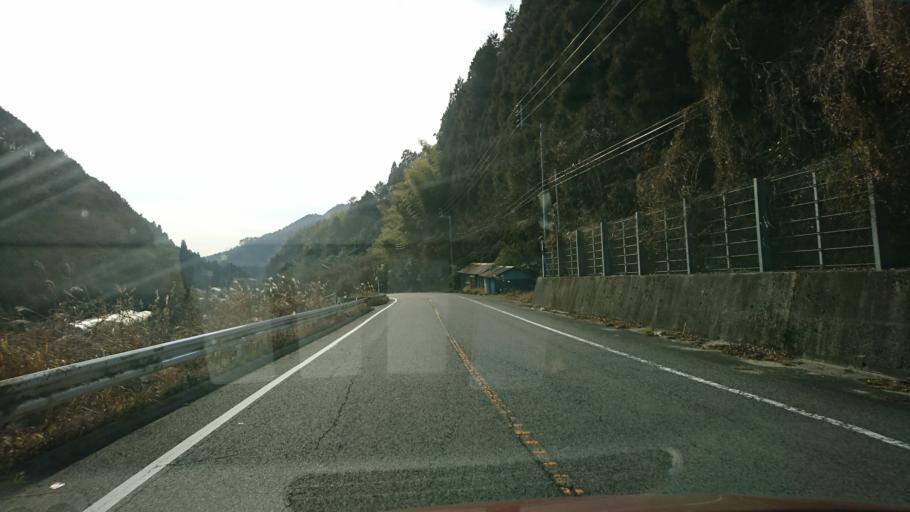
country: JP
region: Ehime
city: Hojo
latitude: 33.9281
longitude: 132.8941
